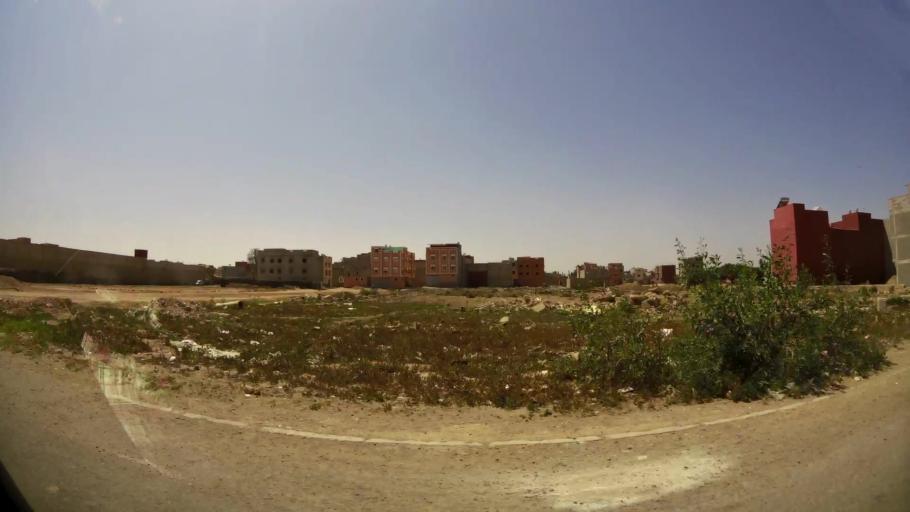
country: MA
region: Souss-Massa-Draa
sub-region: Inezgane-Ait Mellou
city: Inezgane
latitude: 30.3173
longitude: -9.5069
